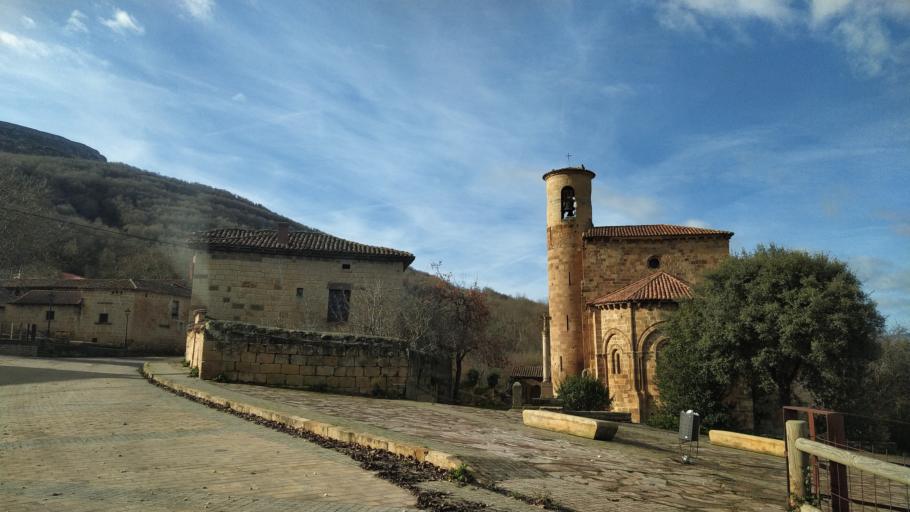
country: ES
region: Cantabria
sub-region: Provincia de Cantabria
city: San Martin de Elines
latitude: 42.8290
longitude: -3.8684
